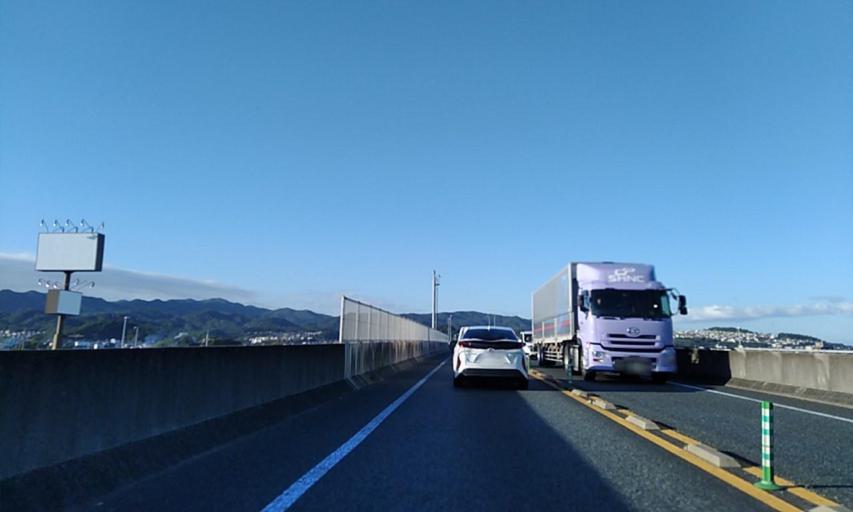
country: JP
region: Wakayama
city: Iwade
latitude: 34.3525
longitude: 135.2593
